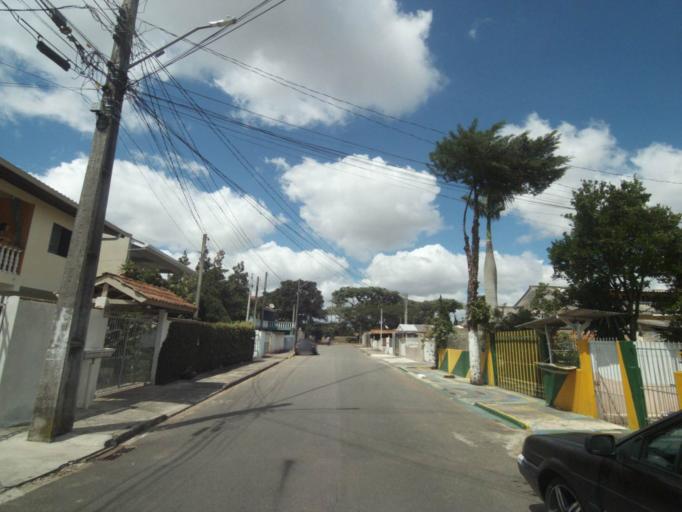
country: BR
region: Parana
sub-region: Pinhais
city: Pinhais
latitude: -25.4422
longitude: -49.2020
